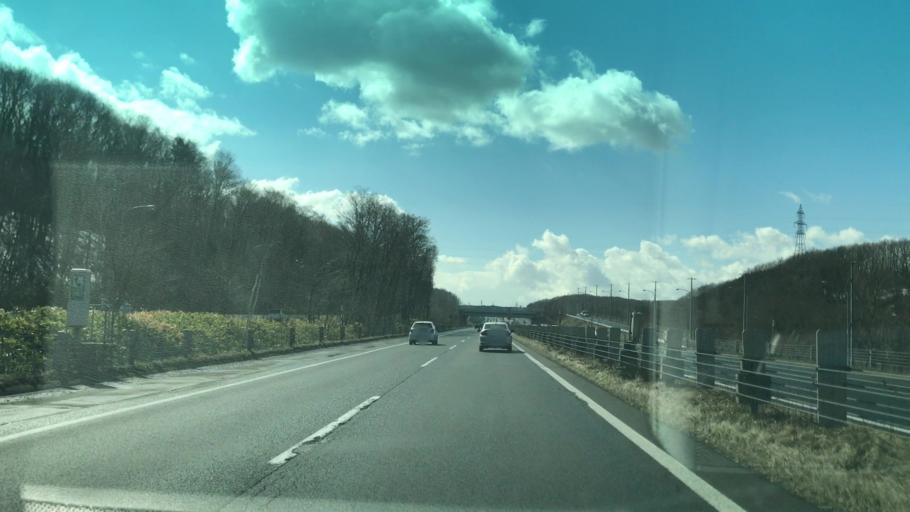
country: JP
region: Hokkaido
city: Kitahiroshima
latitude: 43.0055
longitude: 141.4671
